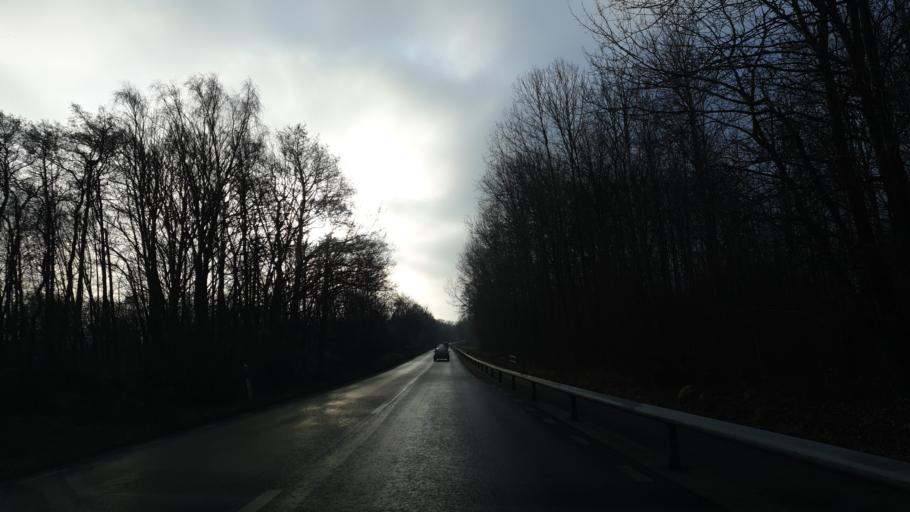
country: SE
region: Blekinge
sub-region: Karlshamns Kommun
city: Morrum
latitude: 56.1365
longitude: 14.6715
